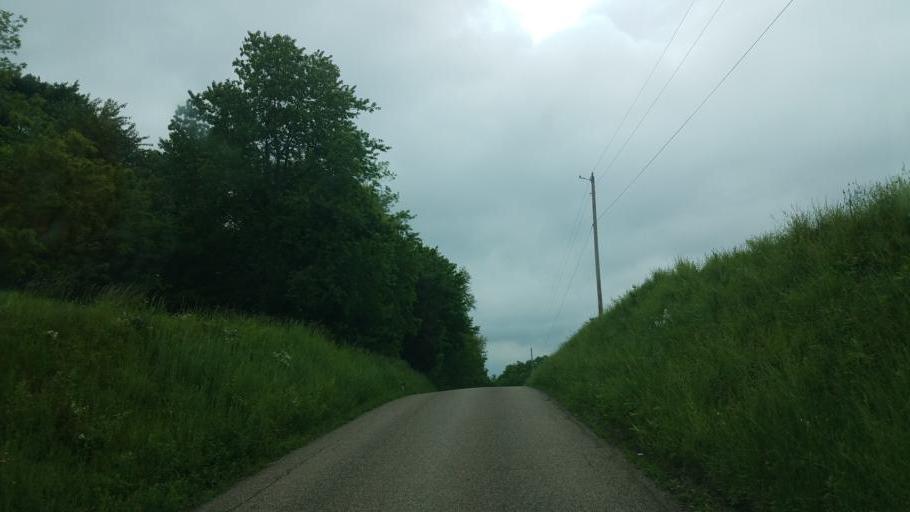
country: US
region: Ohio
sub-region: Ashland County
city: Loudonville
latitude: 40.7122
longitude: -82.3113
